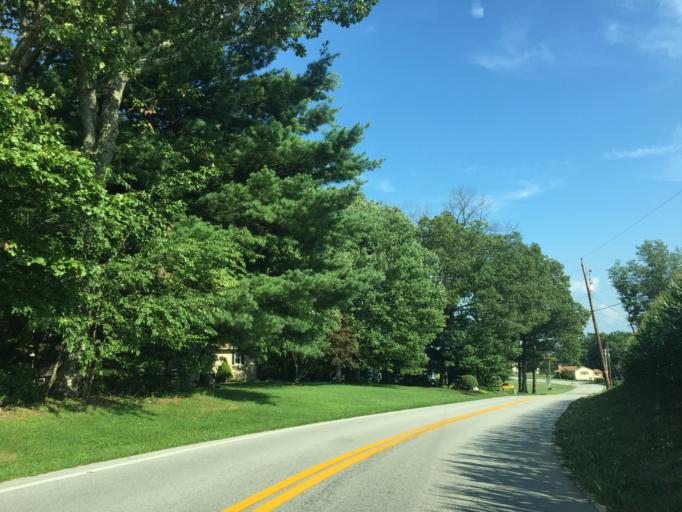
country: US
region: Maryland
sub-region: Carroll County
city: Hampstead
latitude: 39.6473
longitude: -76.8297
